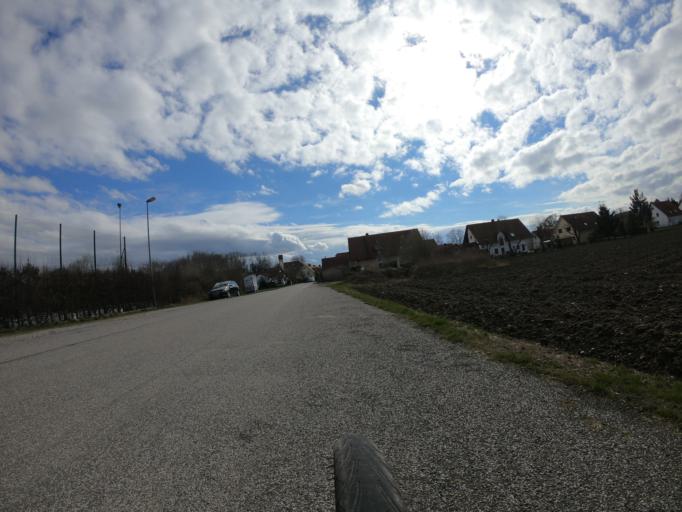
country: DE
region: Bavaria
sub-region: Upper Bavaria
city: Landsberied
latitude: 48.1824
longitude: 11.1867
